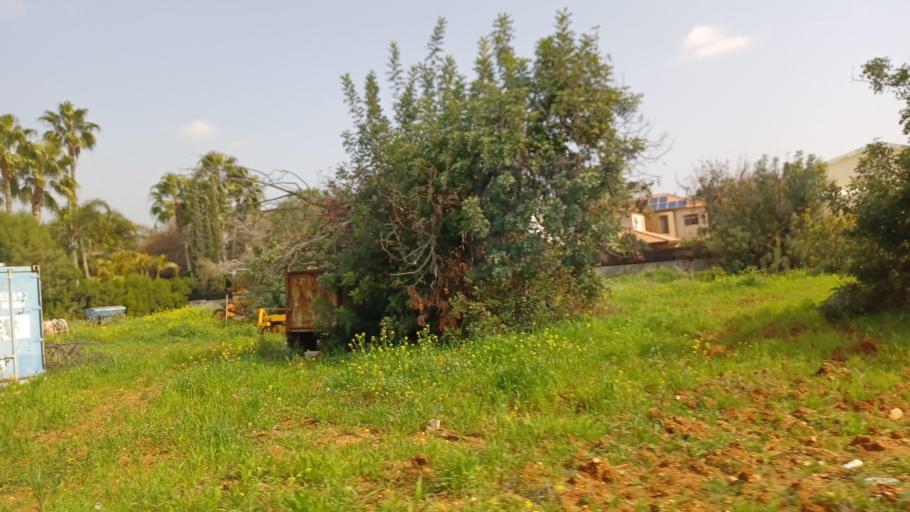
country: CY
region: Limassol
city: Ypsonas
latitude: 34.6849
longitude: 32.9694
